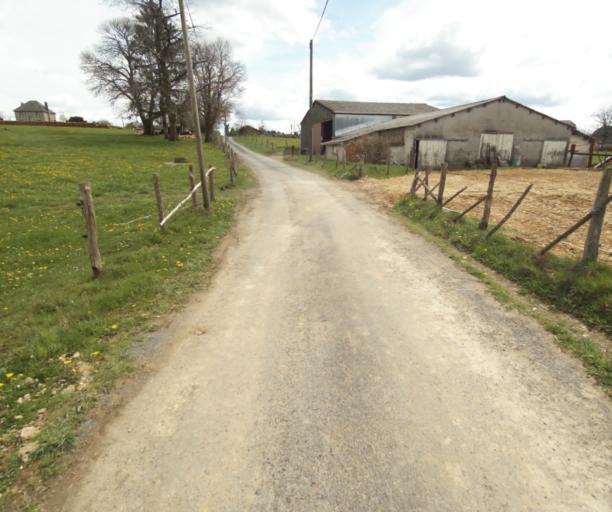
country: FR
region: Limousin
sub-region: Departement de la Correze
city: Laguenne
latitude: 45.2048
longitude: 1.8791
